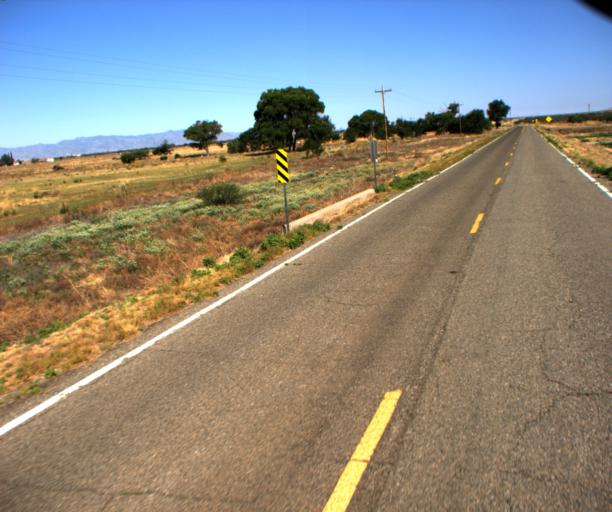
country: US
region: Arizona
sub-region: Graham County
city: Swift Trail Junction
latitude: 32.5878
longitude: -109.9661
